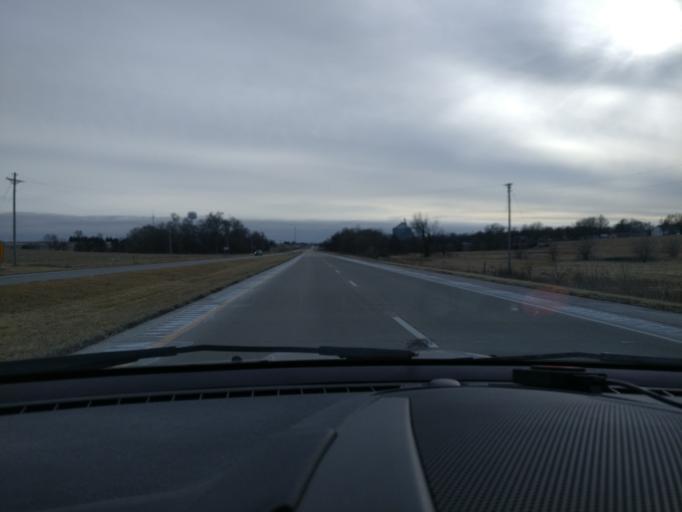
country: US
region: Nebraska
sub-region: Saunders County
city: Wahoo
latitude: 41.0676
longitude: -96.6404
